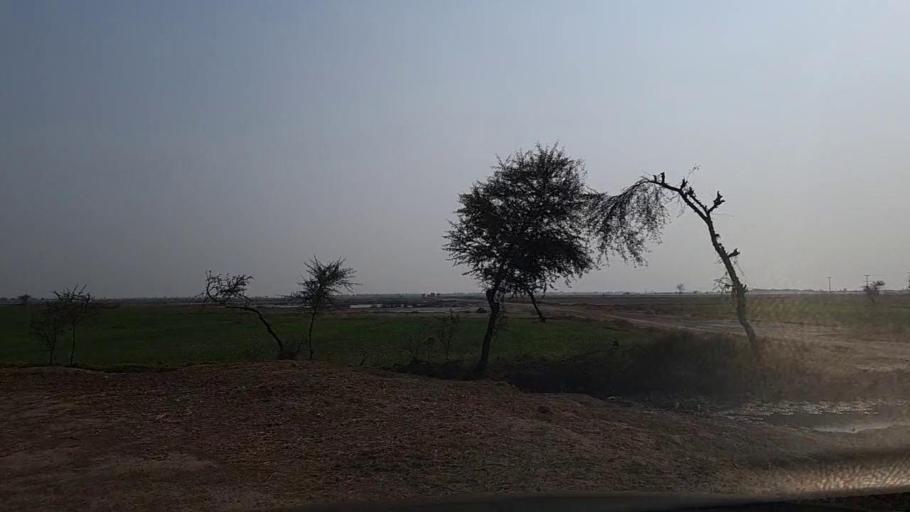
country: PK
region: Sindh
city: Daur
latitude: 26.3905
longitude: 68.4193
